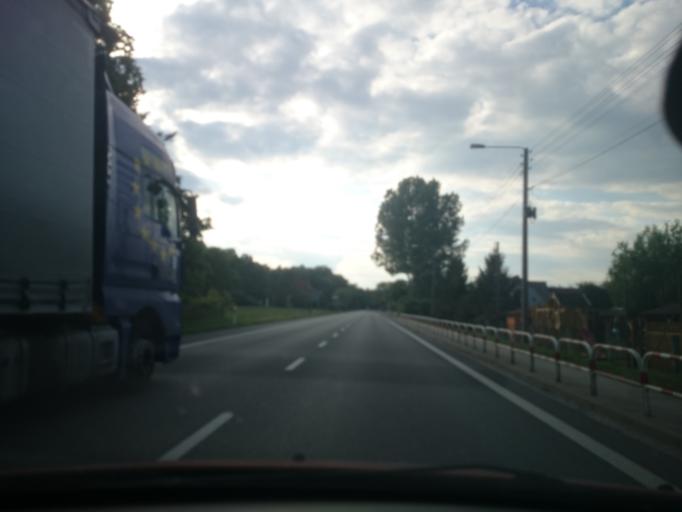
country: PL
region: Opole Voivodeship
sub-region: Powiat opolski
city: Tarnow Opolski
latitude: 50.6025
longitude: 18.0798
